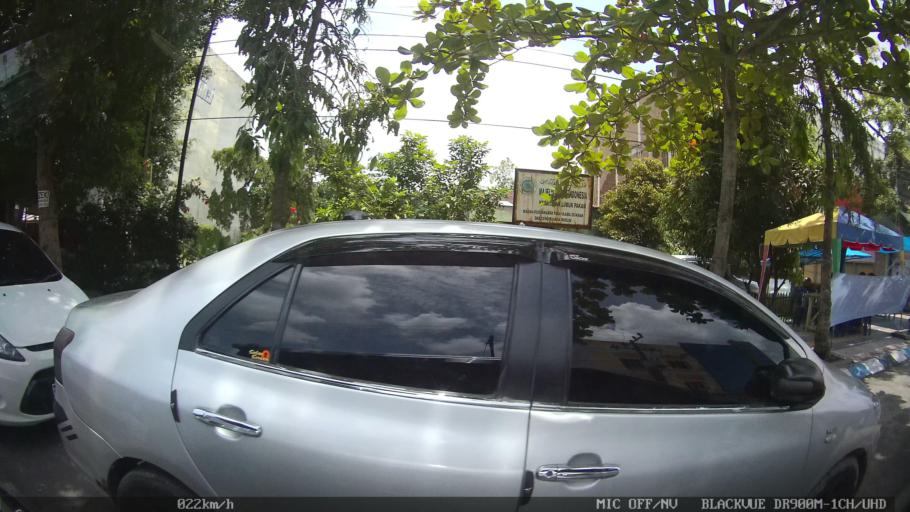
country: ID
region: North Sumatra
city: Percut
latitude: 3.5587
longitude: 98.8686
